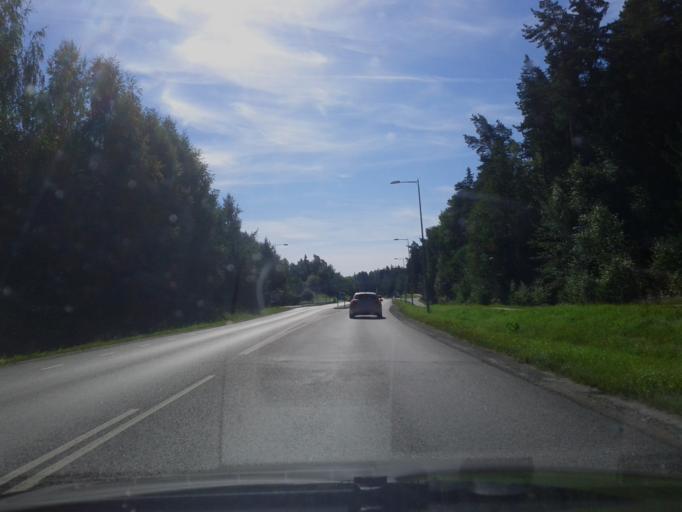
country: SE
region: Stockholm
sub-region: Taby Kommun
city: Taby
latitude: 59.4620
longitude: 18.0747
